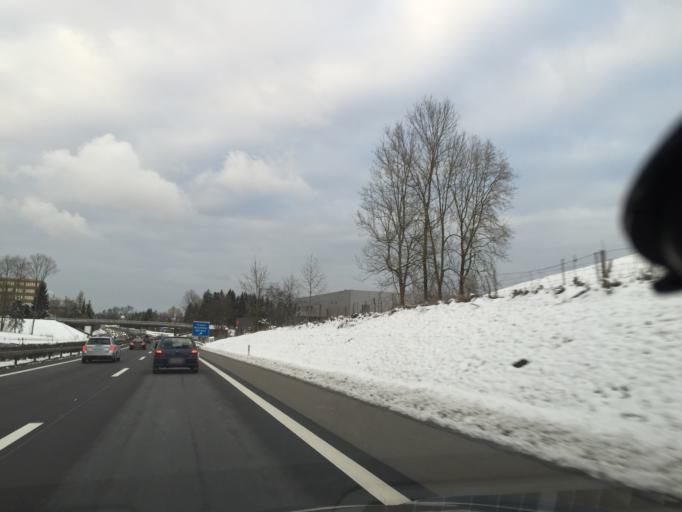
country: CH
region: Zurich
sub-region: Bezirk Horgen
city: Thalwil / Nord
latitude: 47.2989
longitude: 8.5489
